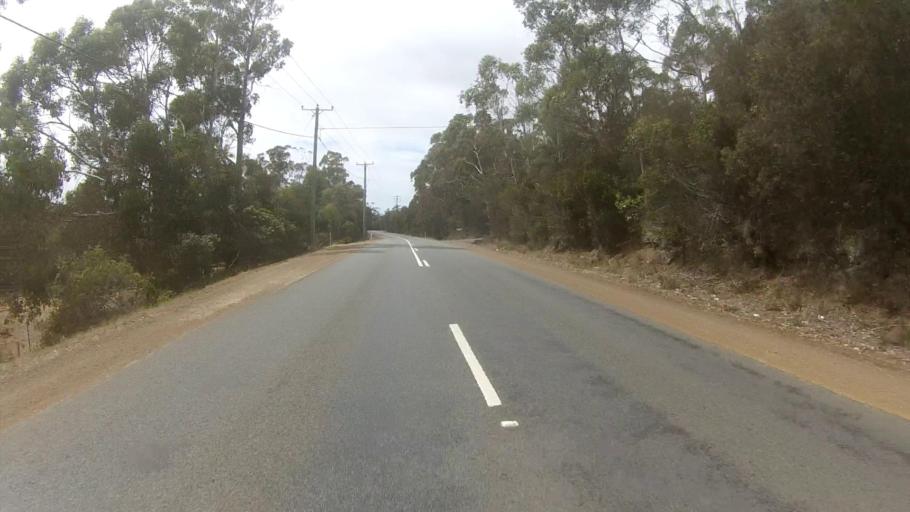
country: AU
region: Tasmania
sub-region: Kingborough
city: Margate
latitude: -43.0049
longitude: 147.2384
